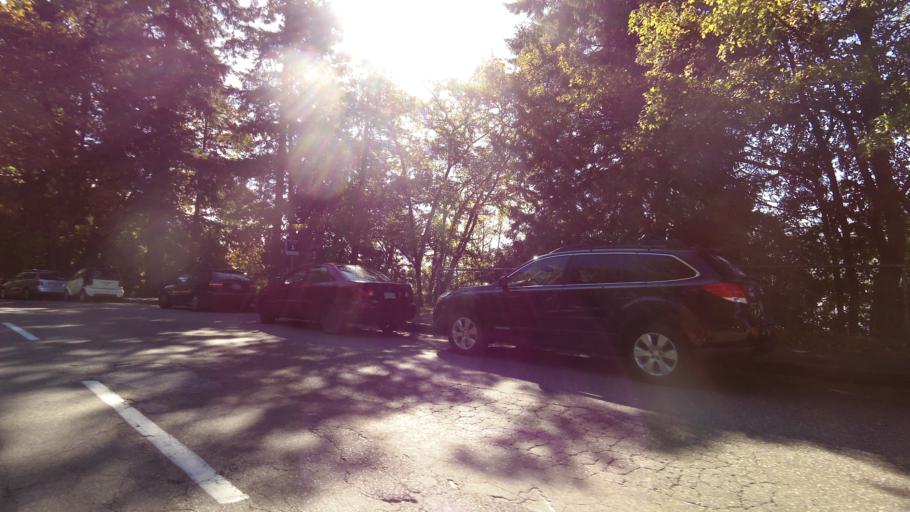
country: CA
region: British Columbia
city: West End
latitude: 49.2971
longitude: -123.1342
